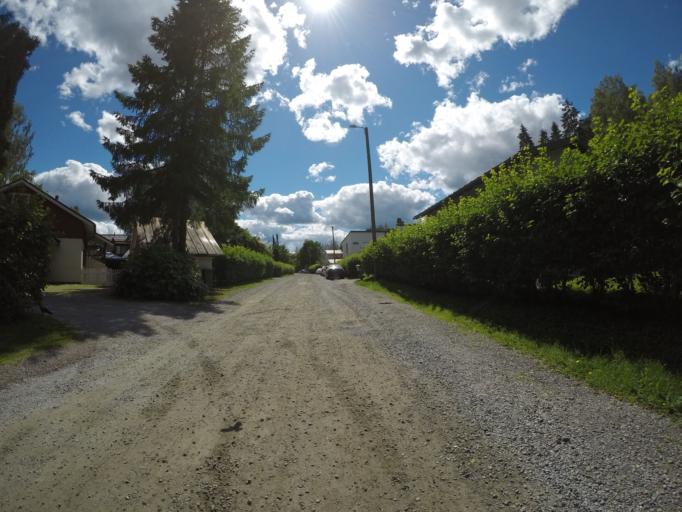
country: FI
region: Haeme
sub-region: Haemeenlinna
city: Haemeenlinna
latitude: 61.0119
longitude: 24.4453
